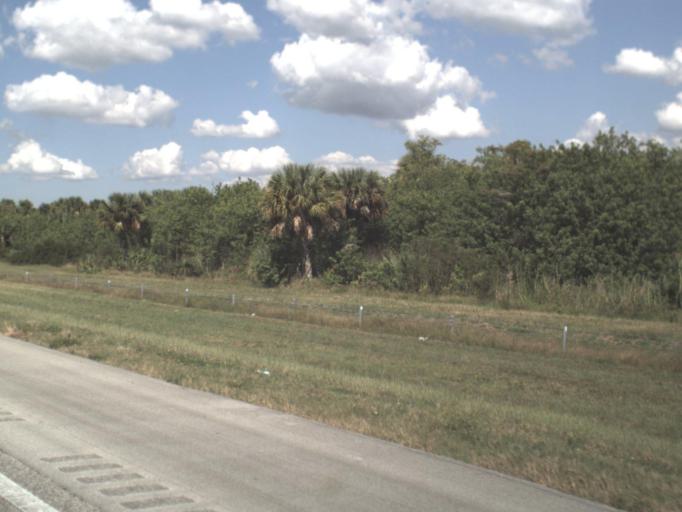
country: US
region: Florida
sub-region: Indian River County
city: West Vero Corridor
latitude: 27.5107
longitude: -80.5889
